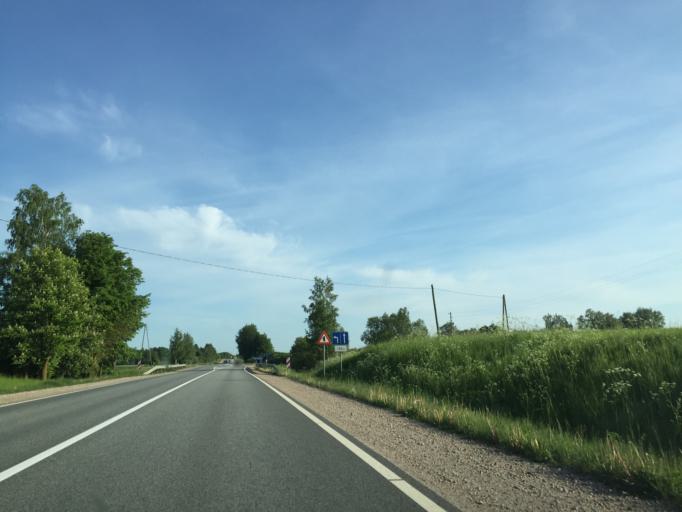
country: LV
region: Bauskas Rajons
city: Bauska
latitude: 56.4956
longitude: 24.1755
